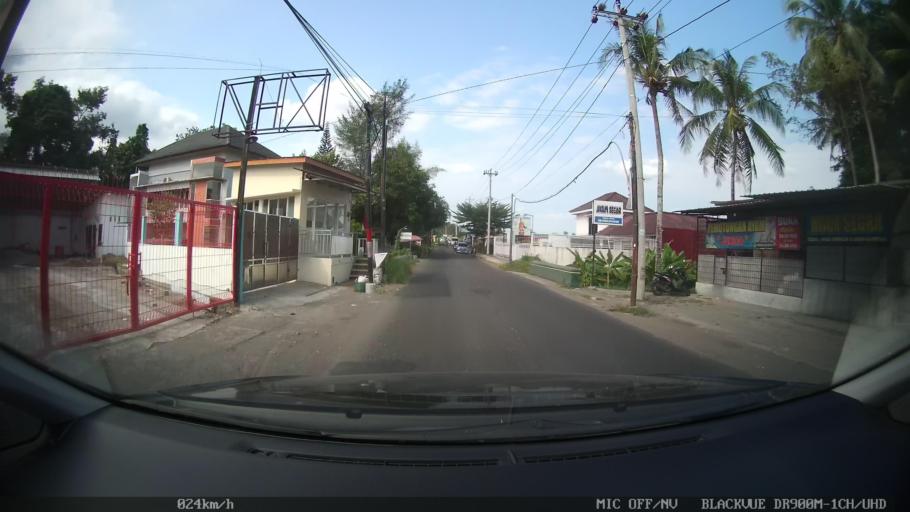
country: ID
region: Daerah Istimewa Yogyakarta
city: Melati
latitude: -7.7304
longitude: 110.4067
